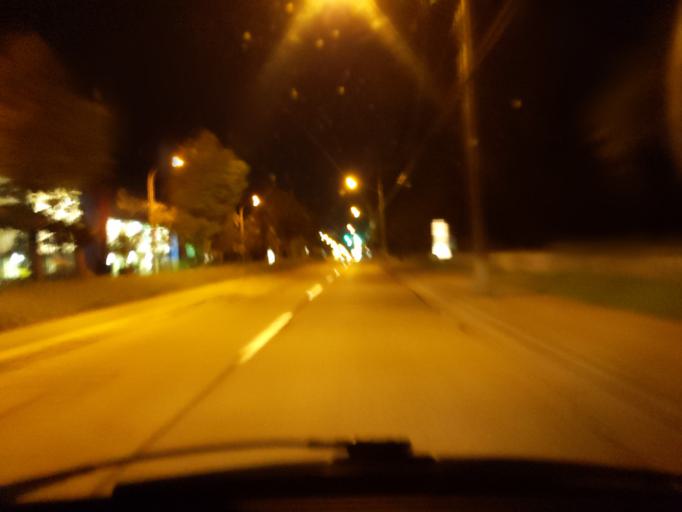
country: CA
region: British Columbia
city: Surrey
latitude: 49.1916
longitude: -122.8150
